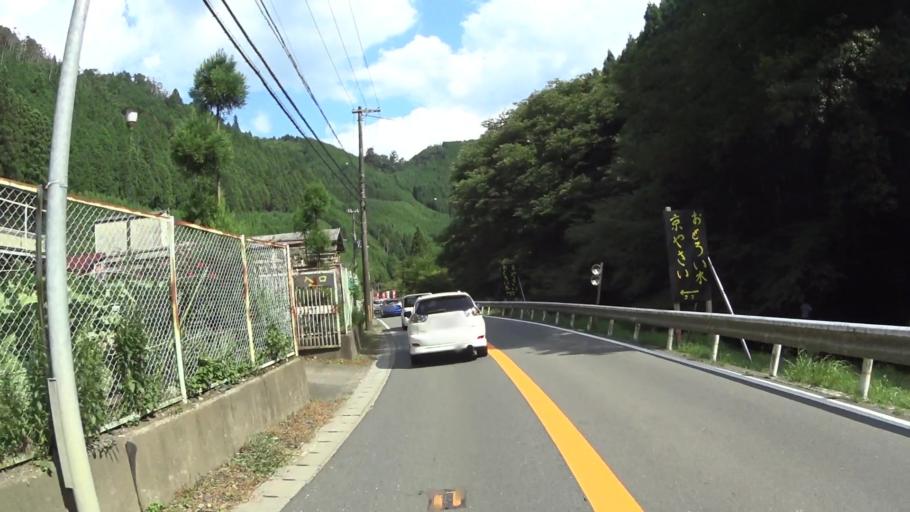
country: JP
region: Kyoto
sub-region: Kyoto-shi
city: Kamigyo-ku
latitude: 35.1086
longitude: 135.6776
